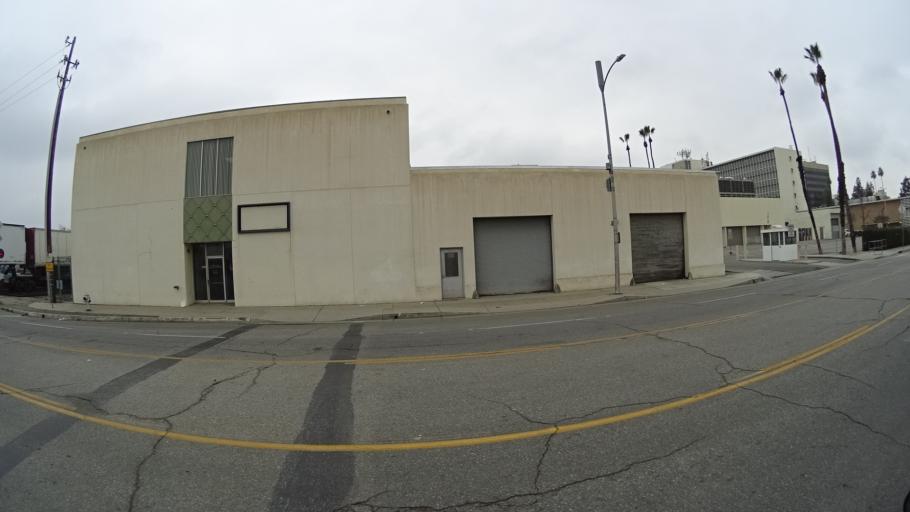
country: US
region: California
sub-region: Kern County
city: Bakersfield
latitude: 35.3717
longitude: -119.0164
